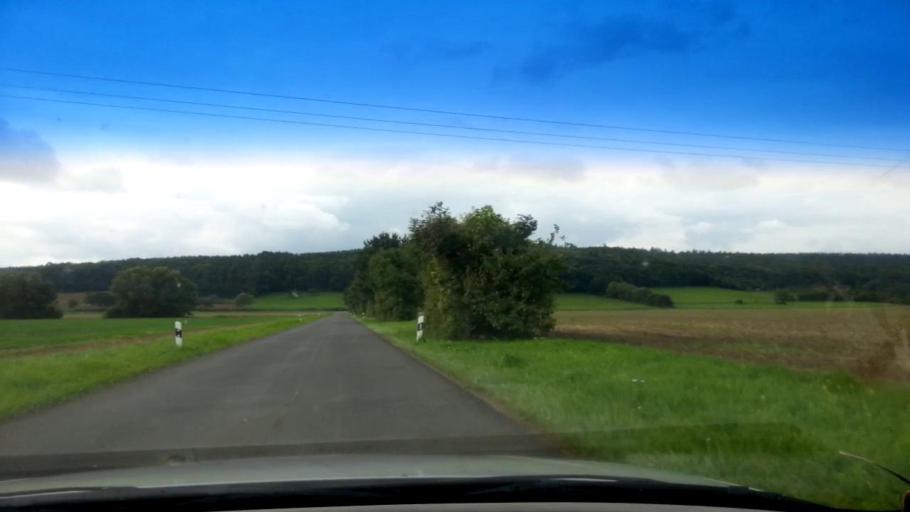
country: DE
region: Bavaria
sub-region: Upper Franconia
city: Zapfendorf
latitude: 50.0406
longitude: 10.9268
